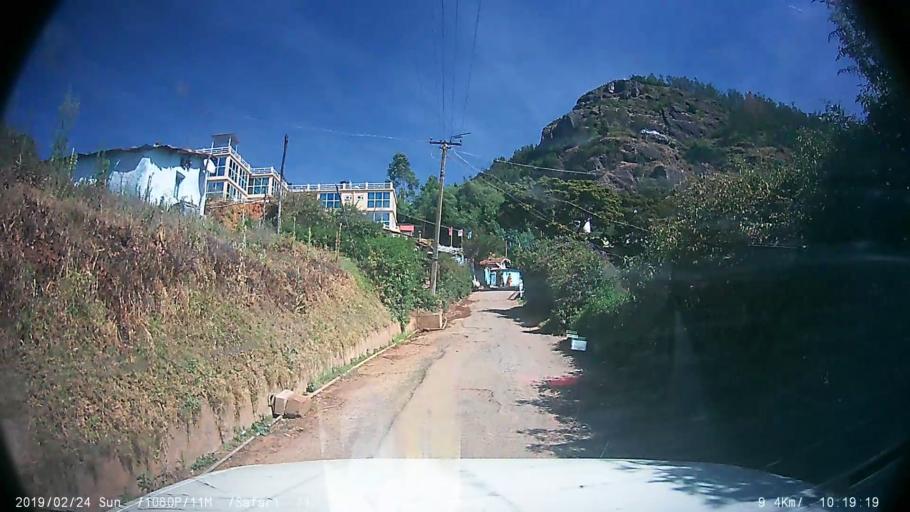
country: IN
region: Tamil Nadu
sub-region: Nilgiri
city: Ooty
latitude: 11.3864
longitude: 76.7197
